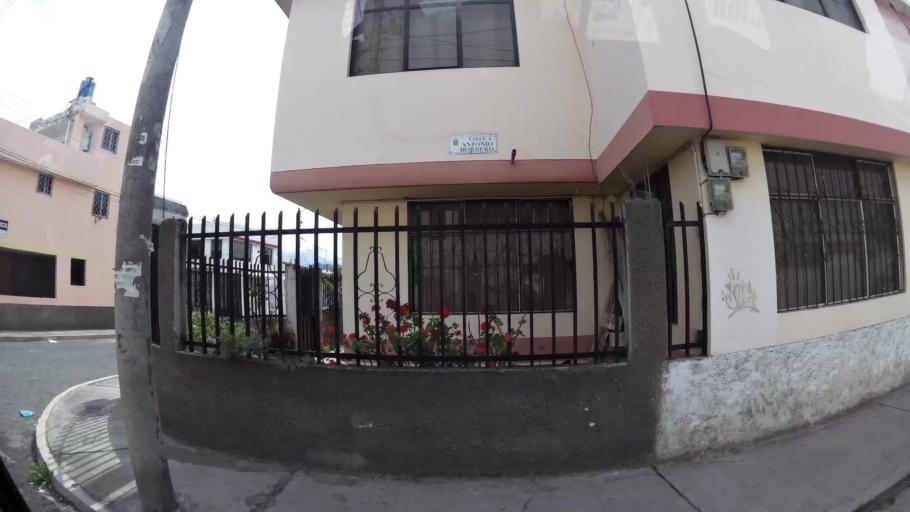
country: EC
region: Cotopaxi
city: Latacunga
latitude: -0.9232
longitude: -78.6219
